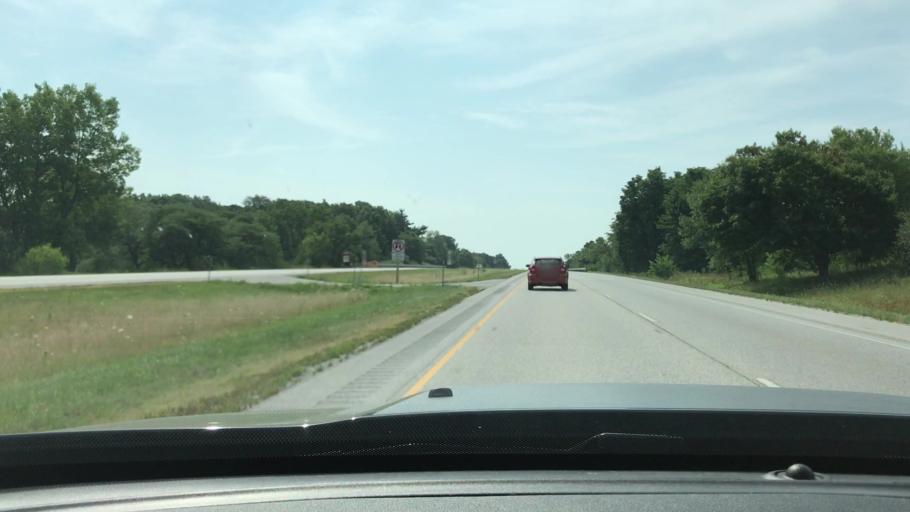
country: US
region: Illinois
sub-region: Henry County
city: Green Rock
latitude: 41.4543
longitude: -90.3752
